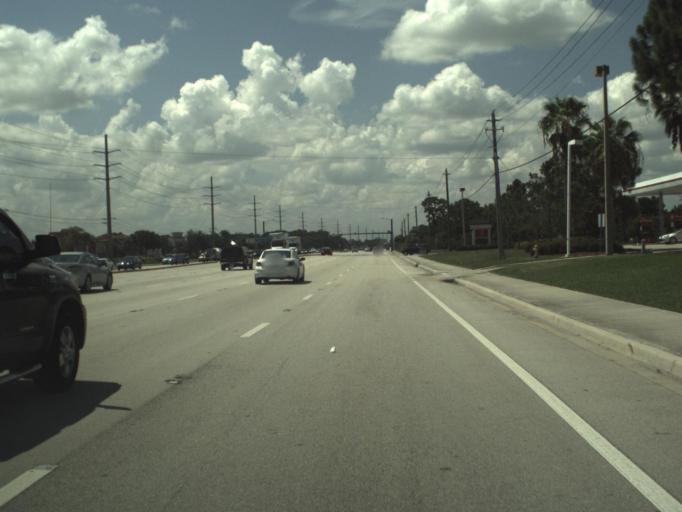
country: US
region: Florida
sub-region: Martin County
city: North River Shores
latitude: 27.2565
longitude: -80.2793
